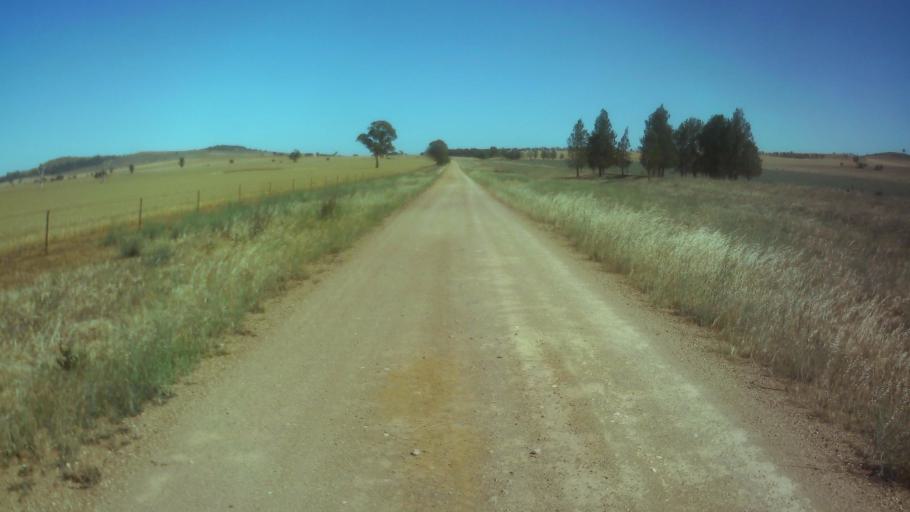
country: AU
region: New South Wales
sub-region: Weddin
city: Grenfell
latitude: -33.9756
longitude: 148.3227
